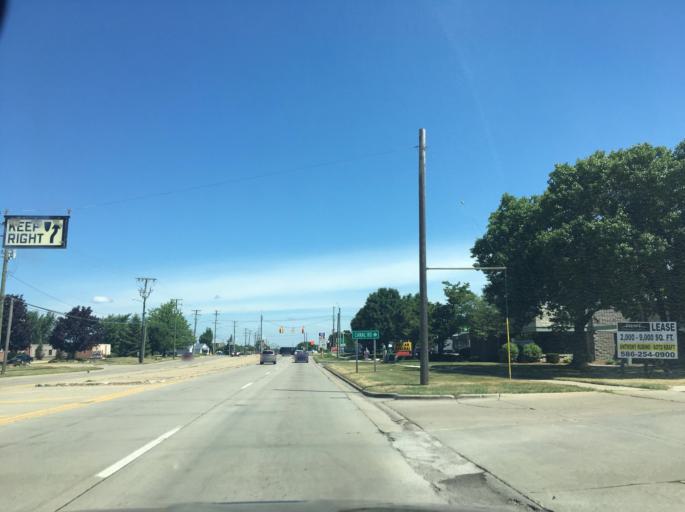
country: US
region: Michigan
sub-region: Macomb County
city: Clinton
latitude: 42.6082
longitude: -82.9724
